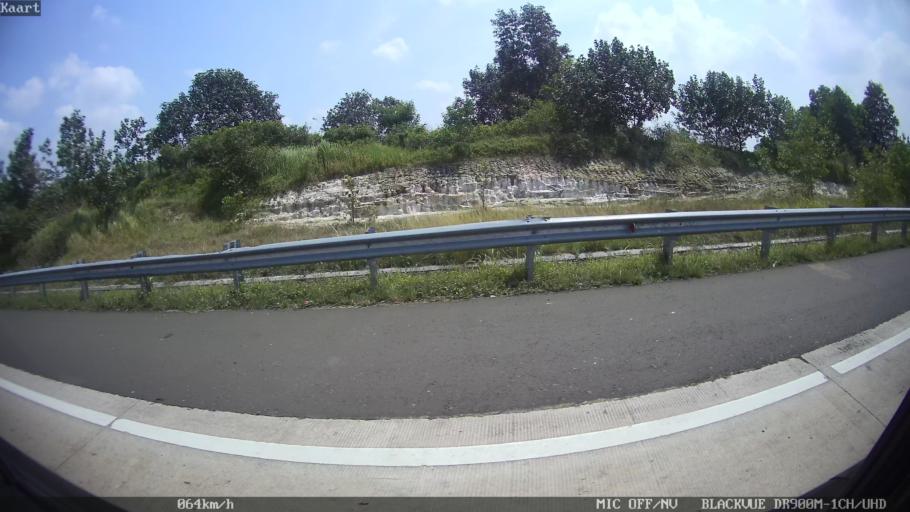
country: ID
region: Lampung
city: Kedaton
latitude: -5.3379
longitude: 105.3053
